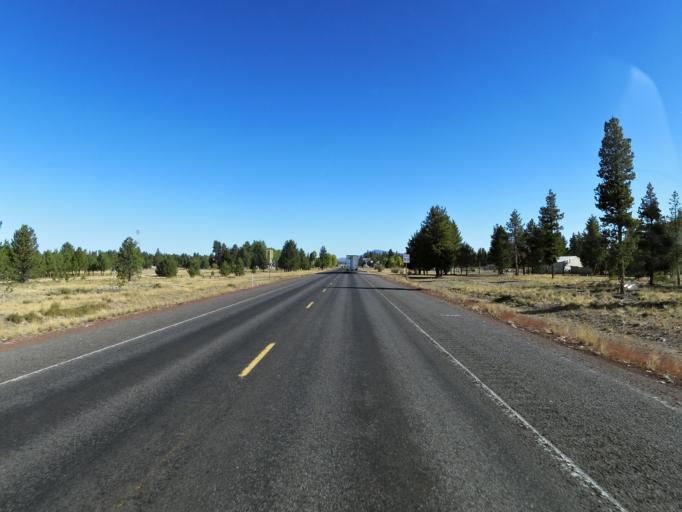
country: US
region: Oregon
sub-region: Deschutes County
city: La Pine
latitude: 43.1305
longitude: -121.8045
